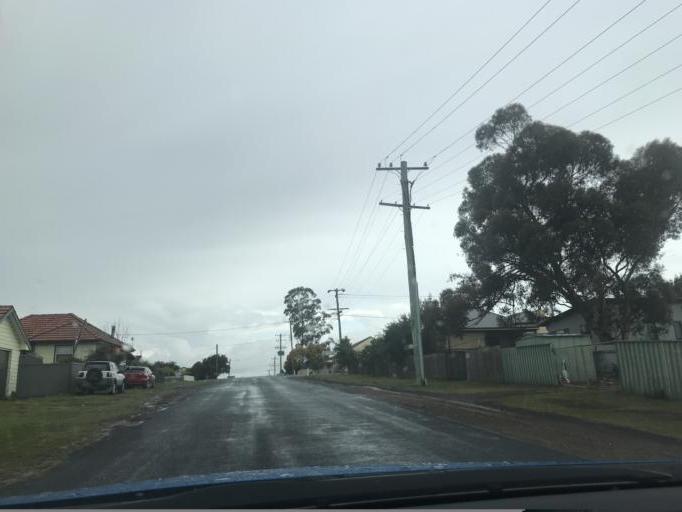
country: AU
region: New South Wales
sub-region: Cessnock
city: Cessnock
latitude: -32.8262
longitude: 151.3495
